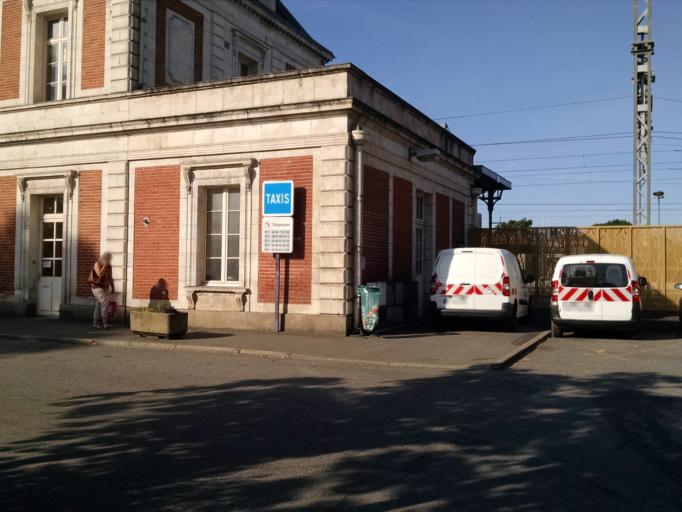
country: FR
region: Pays de la Loire
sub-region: Departement de la Loire-Atlantique
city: Clisson
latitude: 47.0863
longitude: -1.2864
